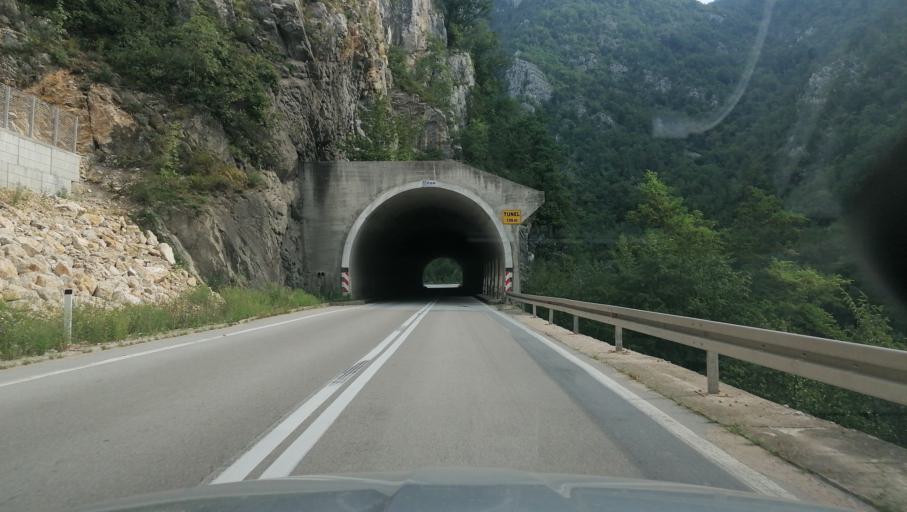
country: BA
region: Federation of Bosnia and Herzegovina
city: Jajce
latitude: 44.4543
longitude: 17.2382
